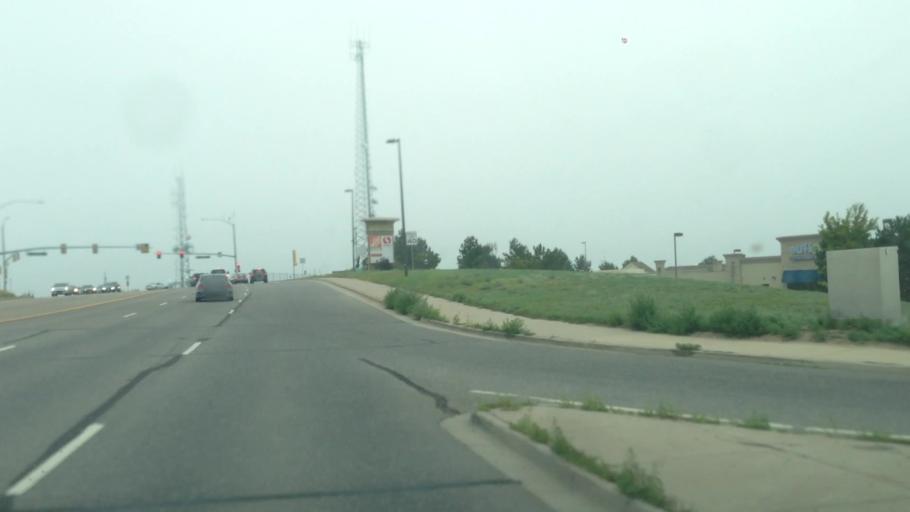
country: US
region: Colorado
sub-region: Douglas County
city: Parker
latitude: 39.6017
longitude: -104.7150
